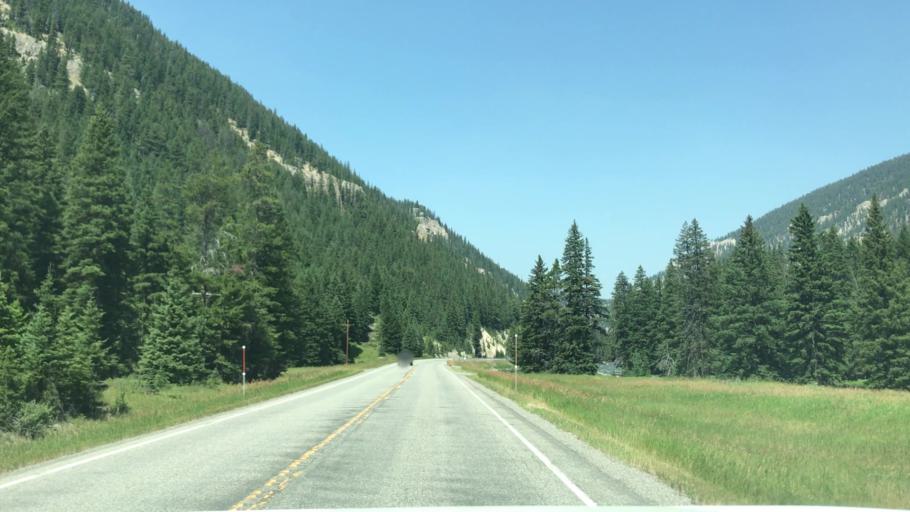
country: US
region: Montana
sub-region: Gallatin County
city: Big Sky
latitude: 45.1259
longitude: -111.2313
